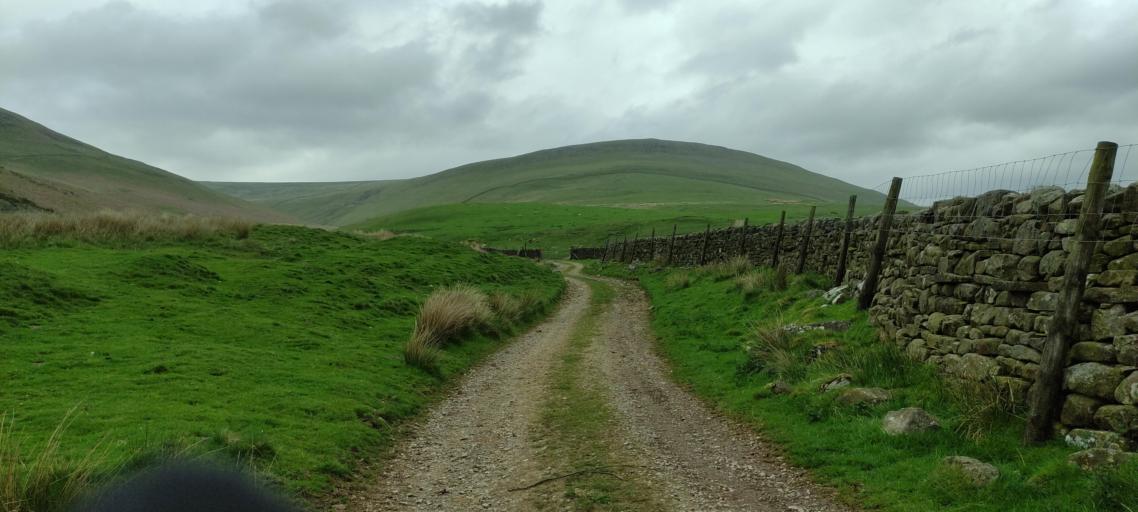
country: GB
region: England
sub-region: Cumbria
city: Appleby-in-Westmorland
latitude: 54.5925
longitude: -2.4191
